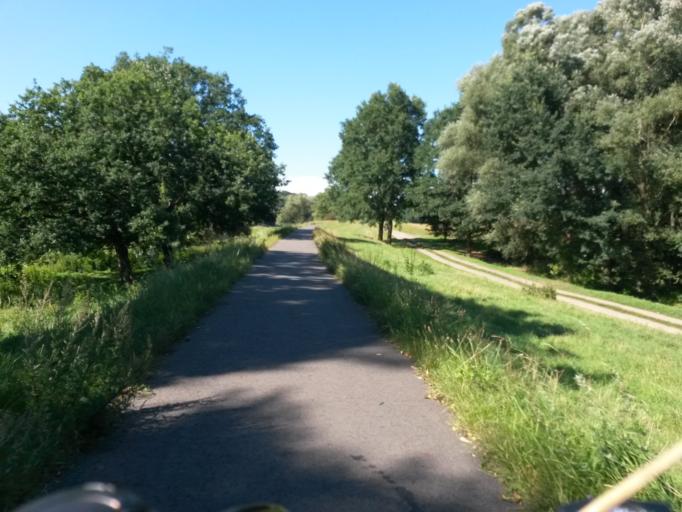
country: DE
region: Brandenburg
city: Schoneberg
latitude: 52.9454
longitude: 14.1124
